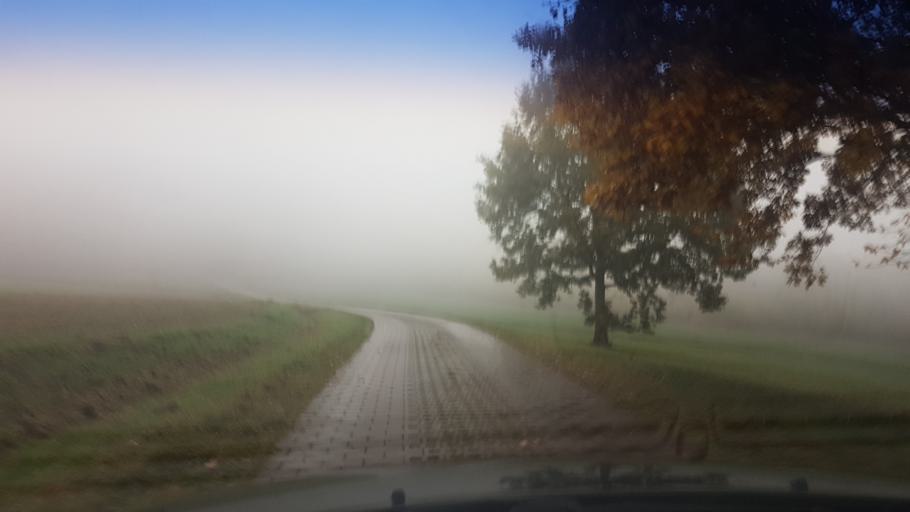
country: DE
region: Bavaria
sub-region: Upper Franconia
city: Baunach
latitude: 50.0015
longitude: 10.8644
